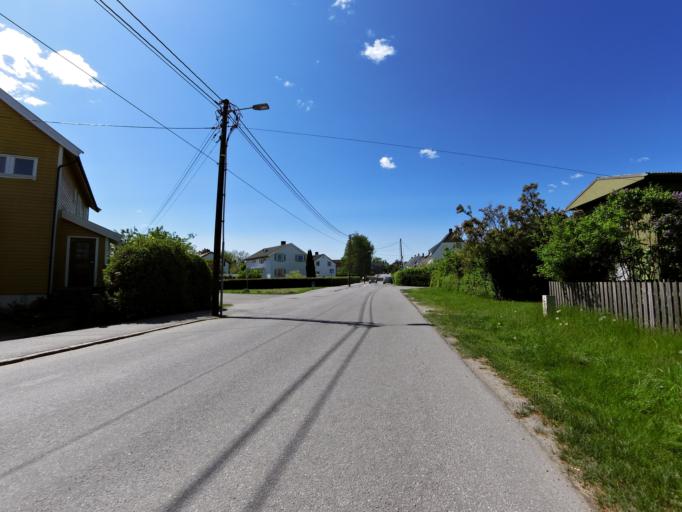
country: NO
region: Ostfold
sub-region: Fredrikstad
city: Fredrikstad
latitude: 59.2325
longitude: 10.9716
